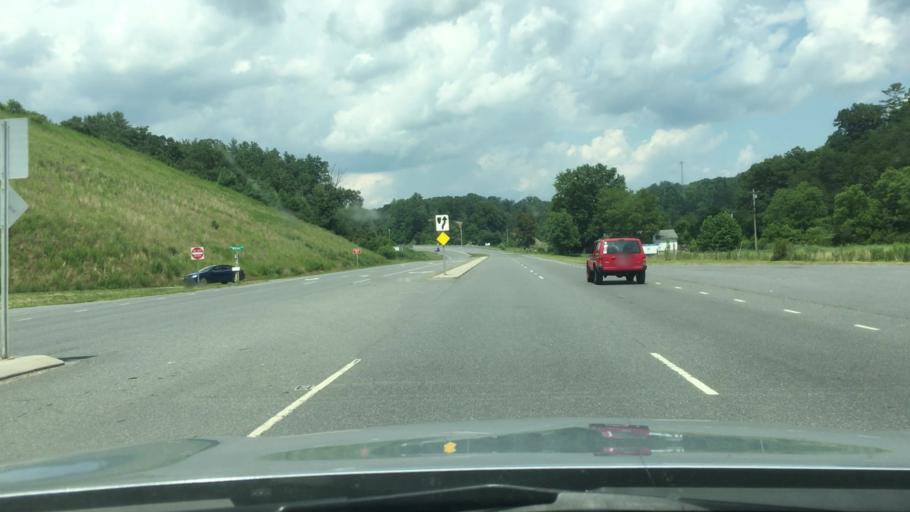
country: US
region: North Carolina
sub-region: Madison County
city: Mars Hill
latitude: 35.8420
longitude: -82.5044
